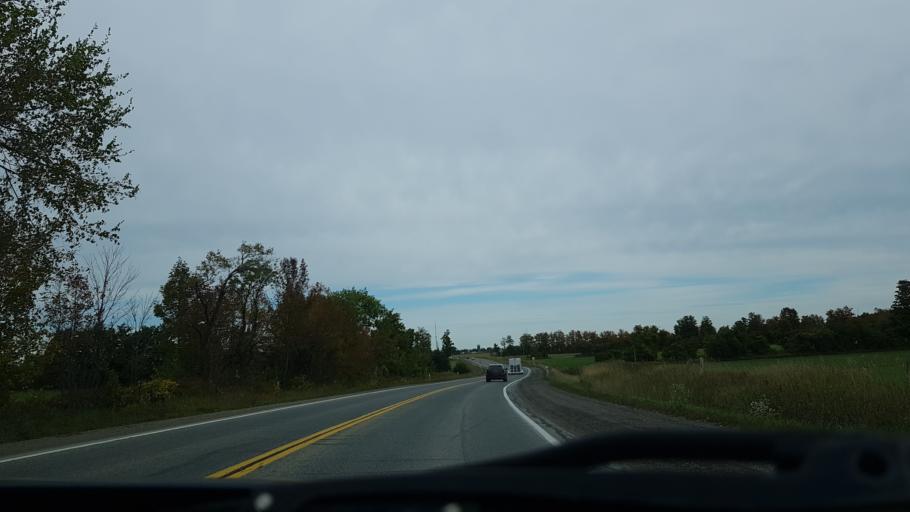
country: CA
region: Ontario
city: Orangeville
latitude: 43.8926
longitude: -79.9597
